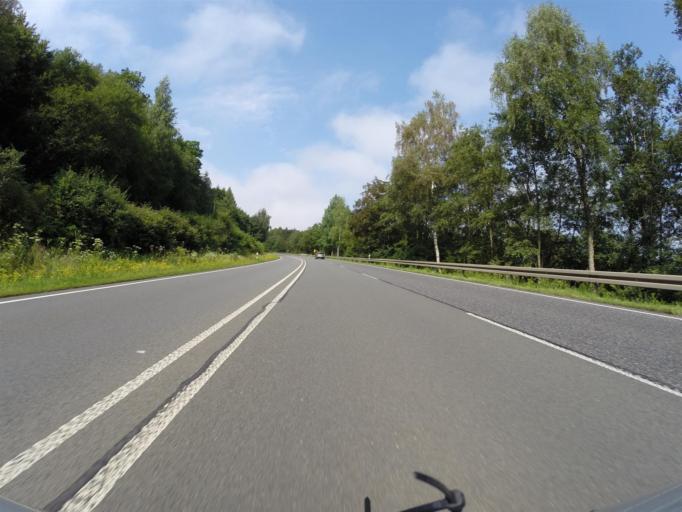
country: DE
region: Hesse
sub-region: Regierungsbezirk Kassel
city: Kaufungen
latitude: 51.2761
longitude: 9.6478
